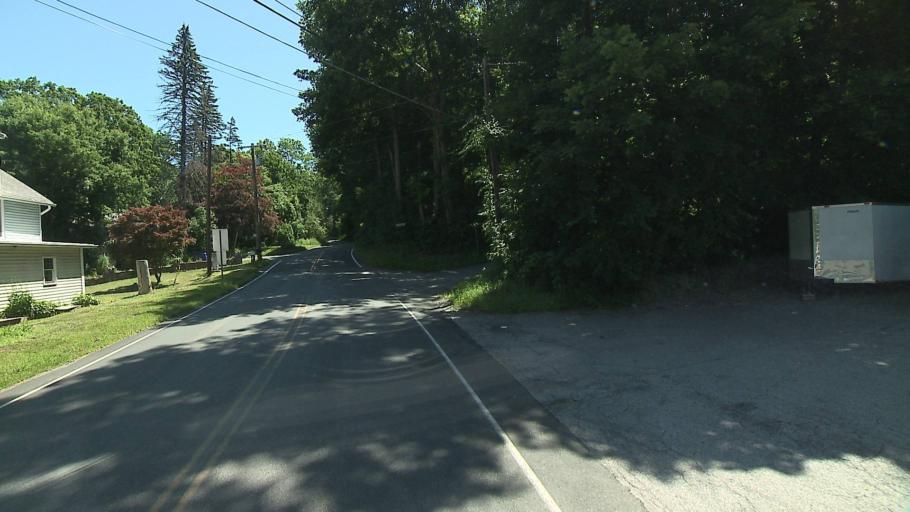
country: US
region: New York
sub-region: Putnam County
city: Putnam Lake
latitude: 41.4550
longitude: -73.5360
